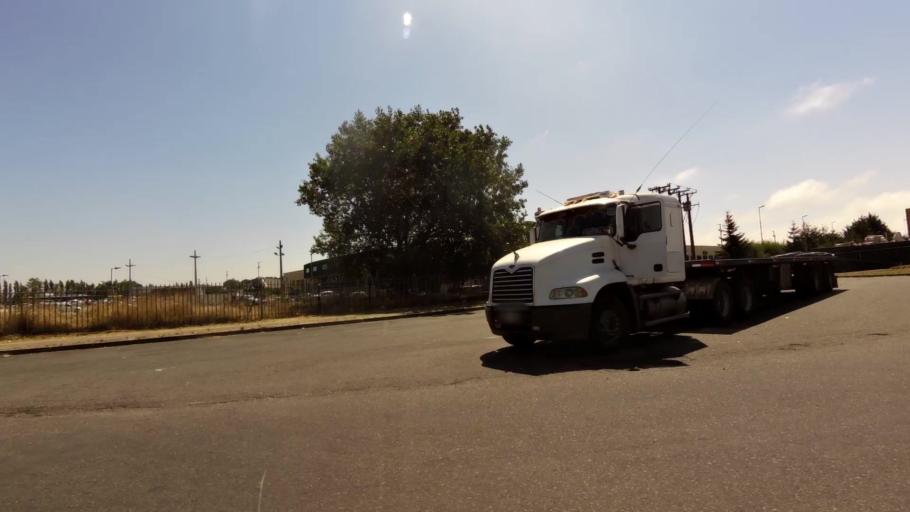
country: CL
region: Biobio
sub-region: Provincia de Concepcion
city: Concepcion
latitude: -36.7997
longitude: -73.0701
